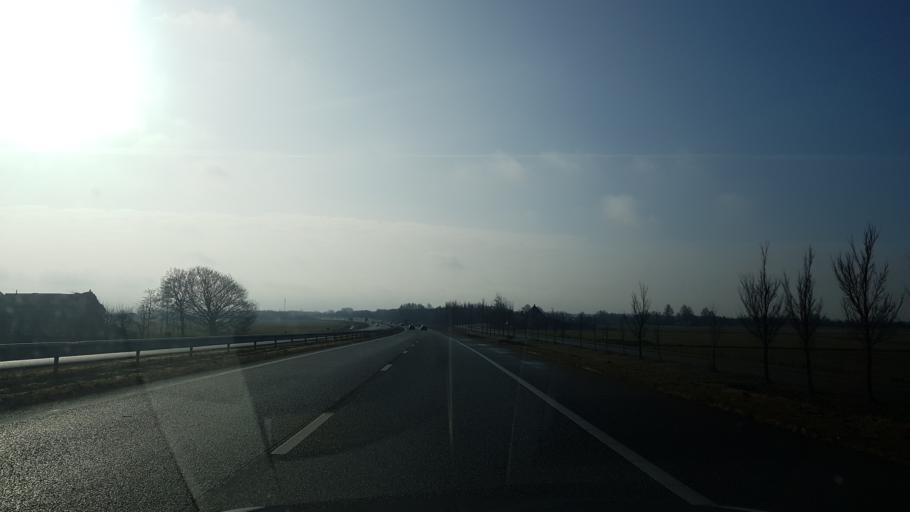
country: NL
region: Friesland
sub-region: Gemeente Skarsterlan
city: Oudehaske
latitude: 53.0037
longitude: 5.8734
